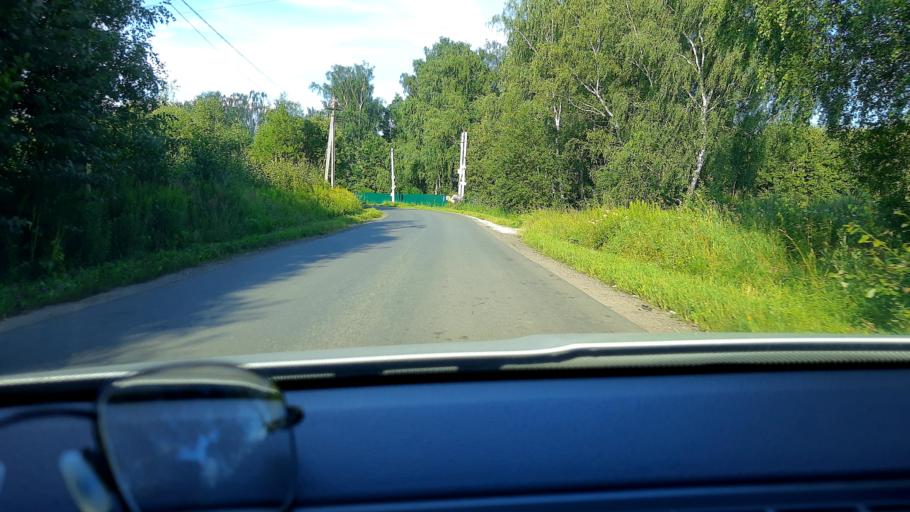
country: RU
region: Moskovskaya
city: Nazar'yevo
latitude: 55.6929
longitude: 37.0627
